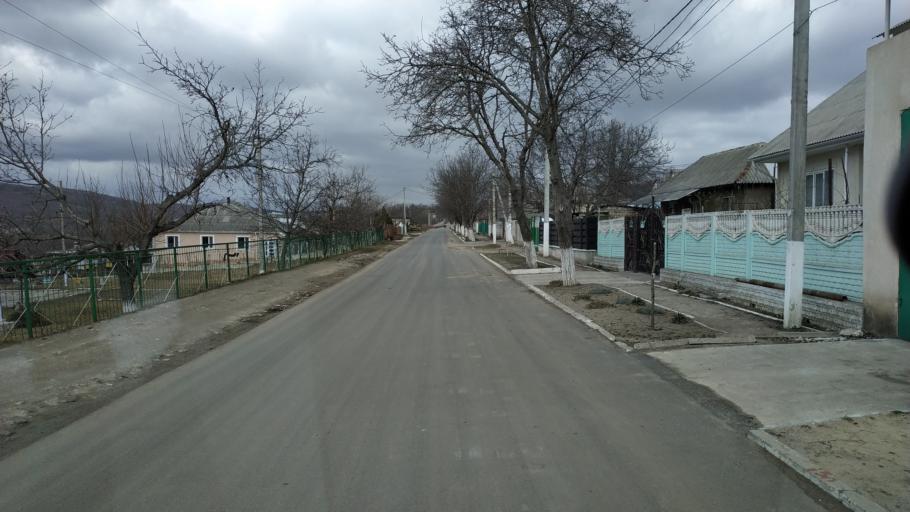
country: MD
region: Stinga Nistrului
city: Bucovat
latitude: 47.2236
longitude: 28.4387
